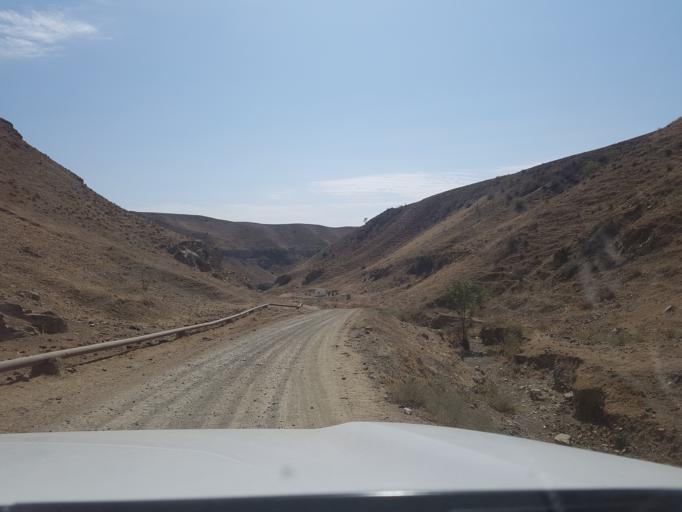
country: TM
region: Ahal
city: Baharly
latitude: 38.2386
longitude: 56.8923
